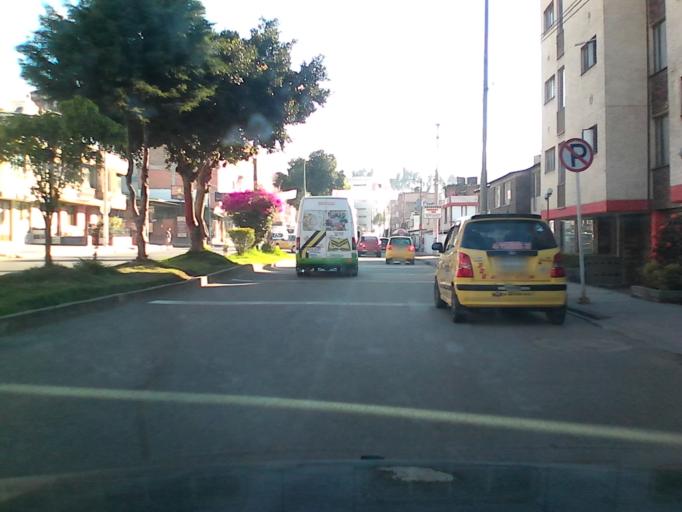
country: CO
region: Boyaca
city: Duitama
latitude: 5.8344
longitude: -73.0345
